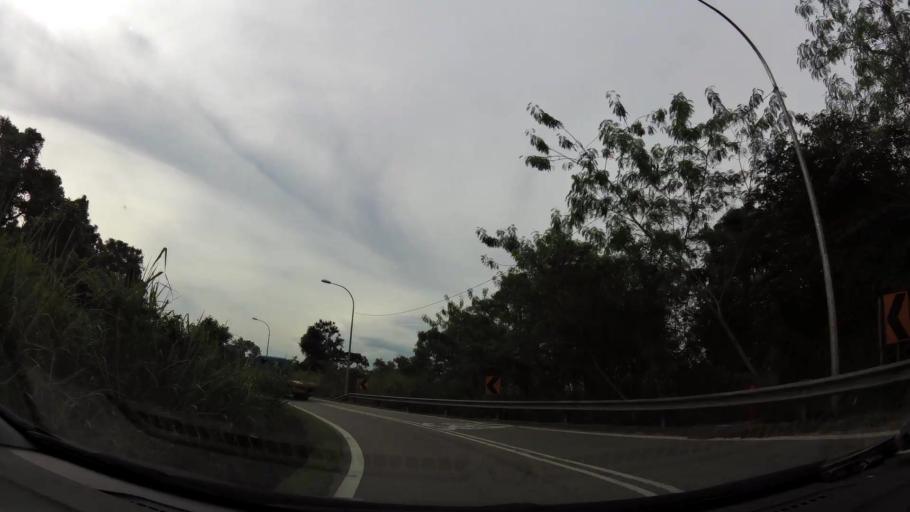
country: MY
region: Johor
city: Johor Bahru
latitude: 1.4172
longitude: 103.7144
